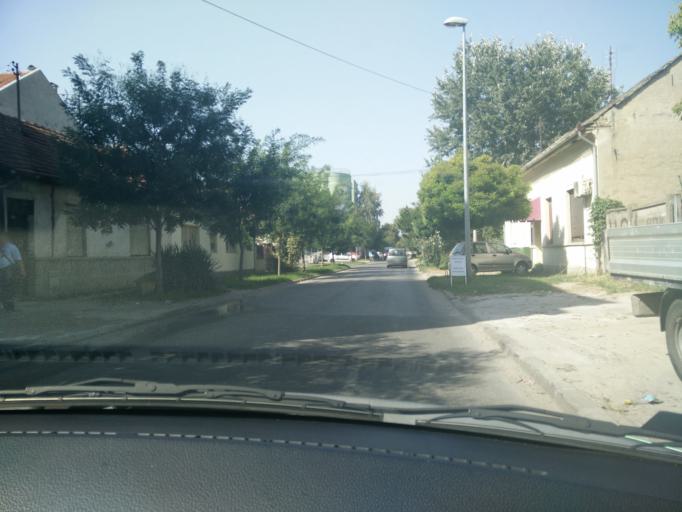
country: RS
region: Autonomna Pokrajina Vojvodina
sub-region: Juznobacki Okrug
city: Novi Sad
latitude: 45.2637
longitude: 19.8516
